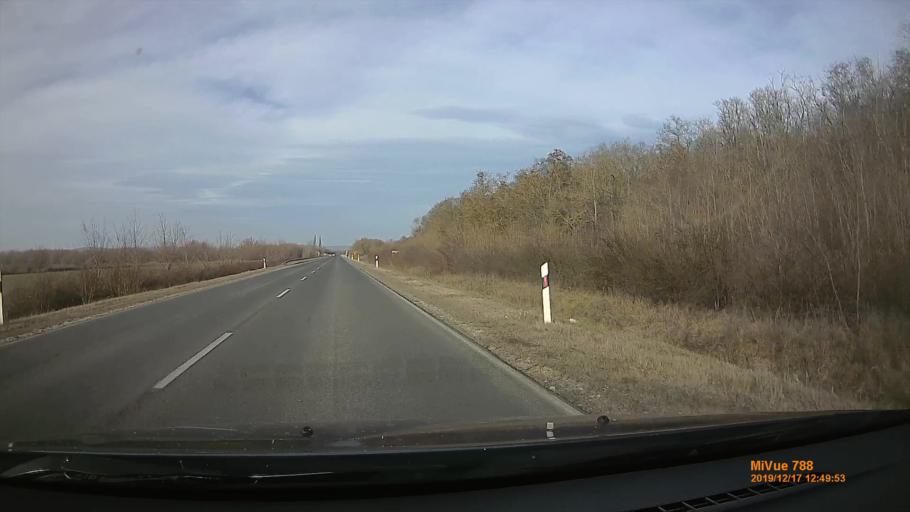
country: HU
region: Somogy
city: Balatonlelle
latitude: 46.7632
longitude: 17.7619
